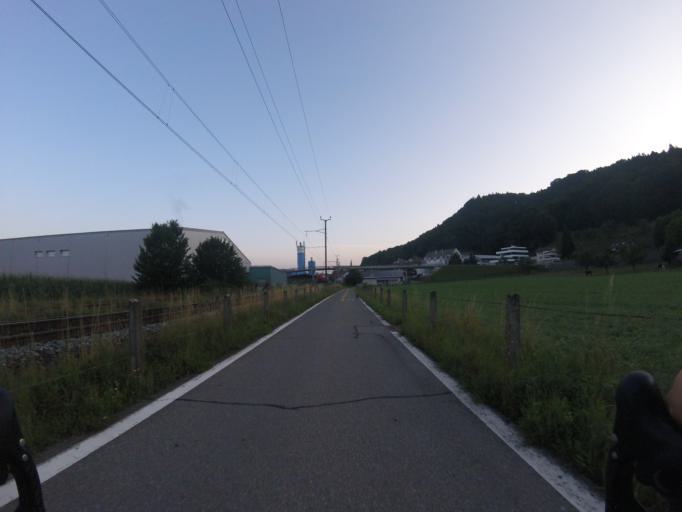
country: CH
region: Bern
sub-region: Thun District
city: Heimberg
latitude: 46.7879
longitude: 7.6073
